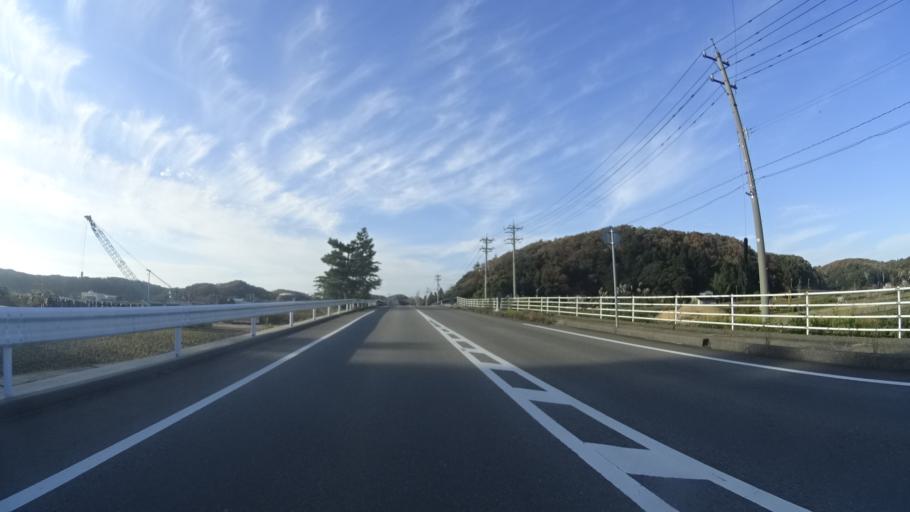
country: JP
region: Ishikawa
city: Hakui
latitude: 37.0199
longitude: 136.7901
